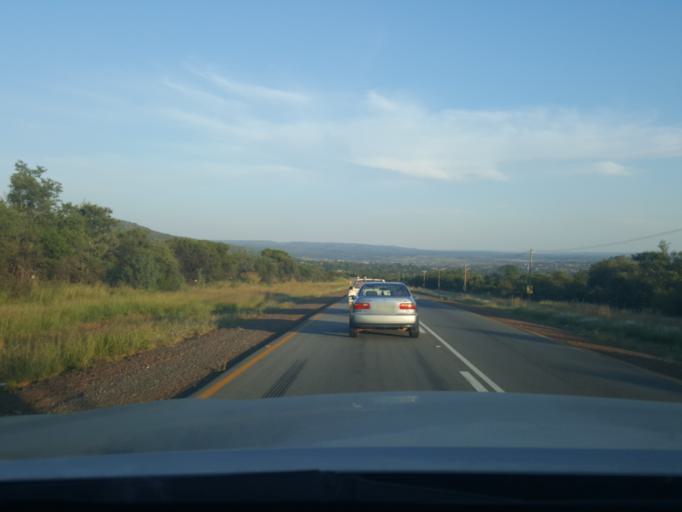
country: ZA
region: North-West
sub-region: Ngaka Modiri Molema District Municipality
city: Zeerust
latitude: -25.5160
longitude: 26.0634
